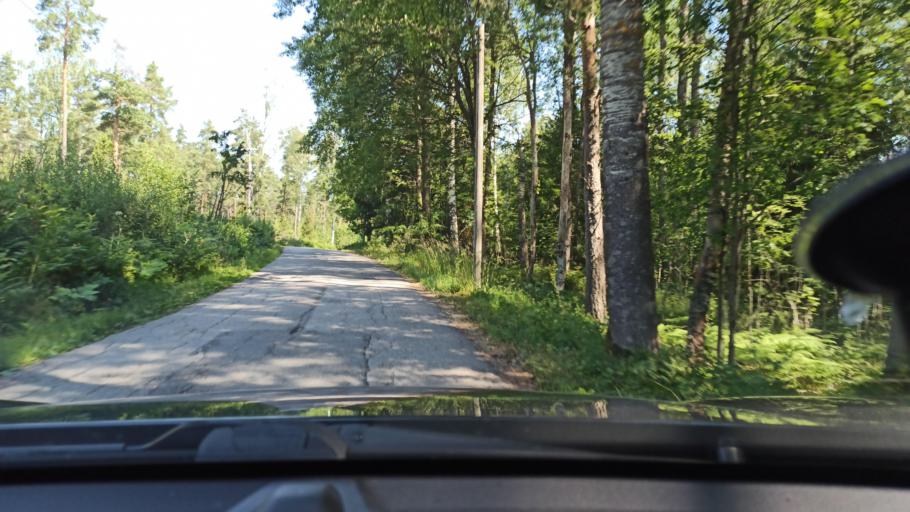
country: FI
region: Uusimaa
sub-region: Helsinki
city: Espoo
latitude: 60.1520
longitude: 24.5670
